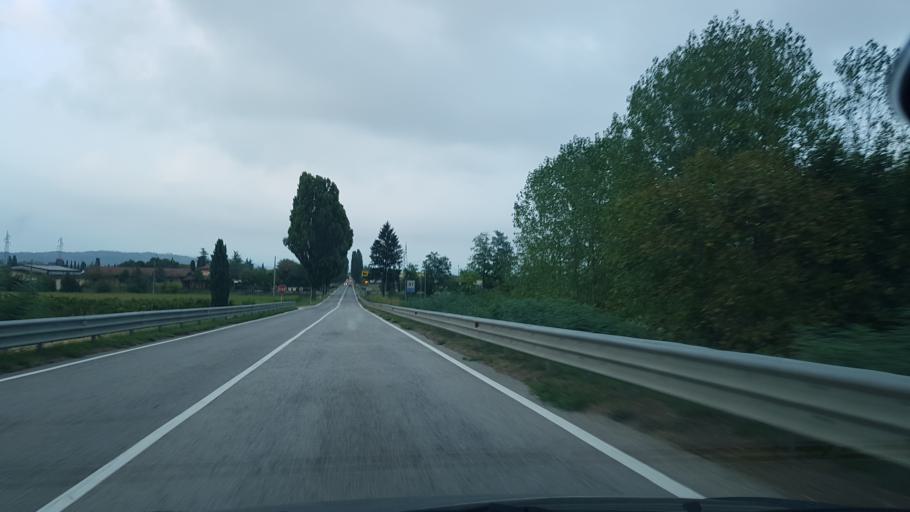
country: IT
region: Friuli Venezia Giulia
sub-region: Provincia di Gorizia
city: Medea
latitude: 45.8948
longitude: 13.4088
